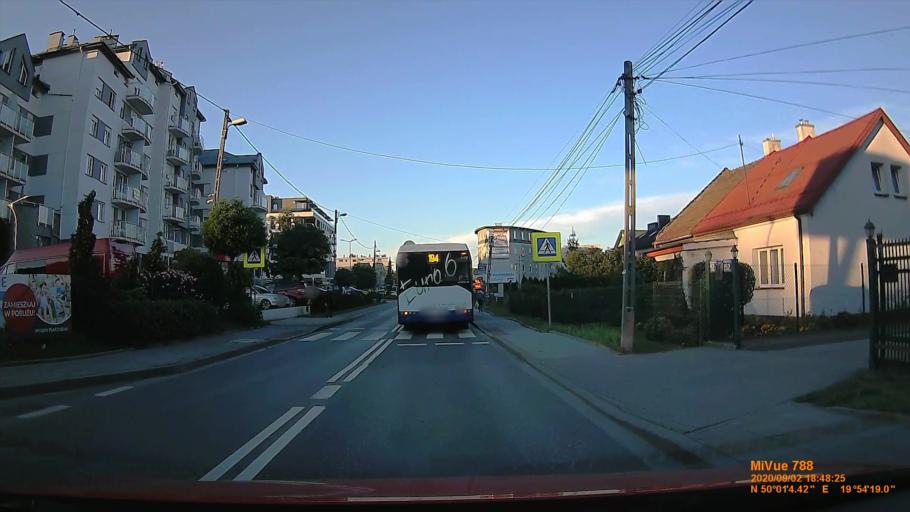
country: PL
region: Lesser Poland Voivodeship
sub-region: Krakow
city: Sidzina
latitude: 50.0181
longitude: 19.9054
